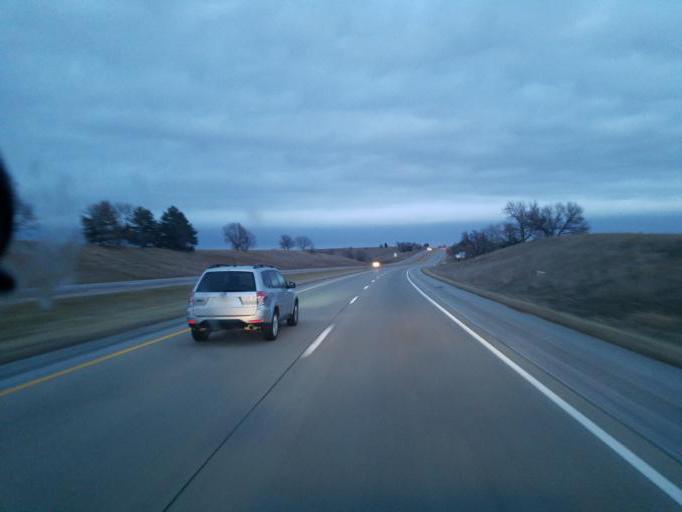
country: US
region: Iowa
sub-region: Cass County
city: Atlantic
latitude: 41.4983
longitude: -95.0975
